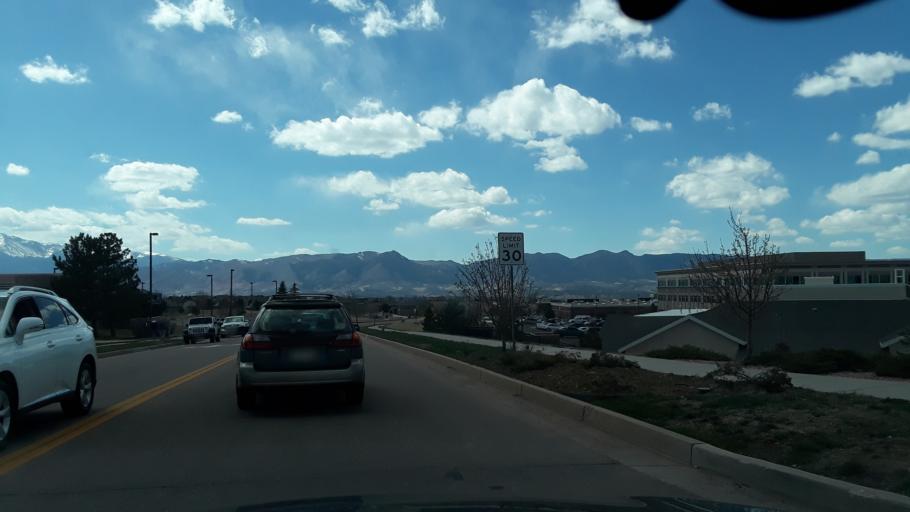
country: US
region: Colorado
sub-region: El Paso County
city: Black Forest
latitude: 38.9637
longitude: -104.7508
